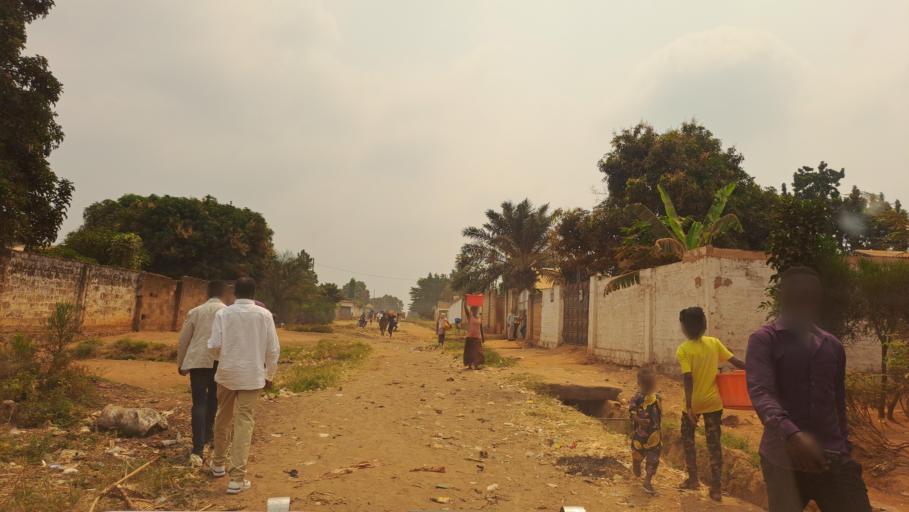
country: CD
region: Kasai-Oriental
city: Mbuji-Mayi
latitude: -6.1202
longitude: 23.6025
